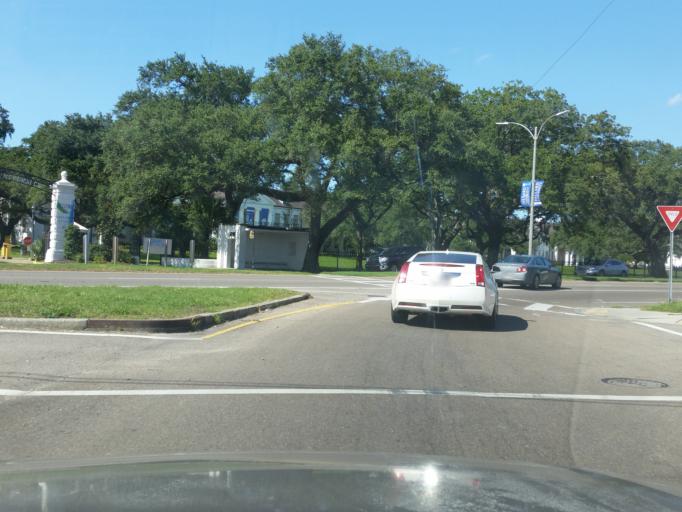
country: US
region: Louisiana
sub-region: Orleans Parish
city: New Orleans
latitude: 29.9933
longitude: -90.0659
